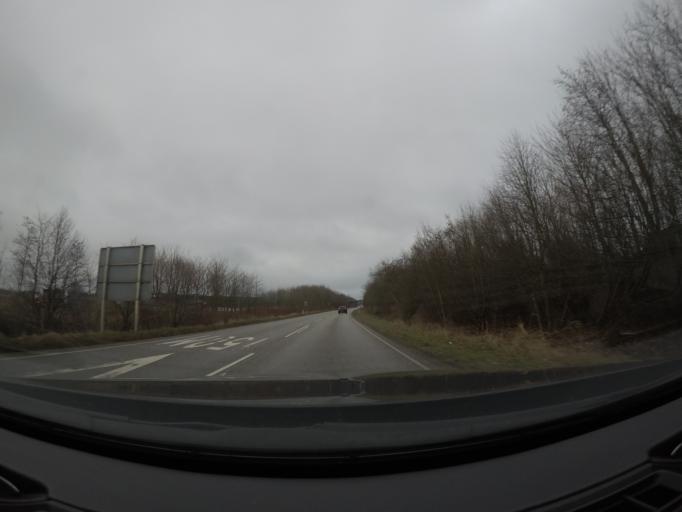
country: DK
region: South Denmark
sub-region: Kolding Kommune
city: Kolding
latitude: 55.5493
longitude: 9.4948
